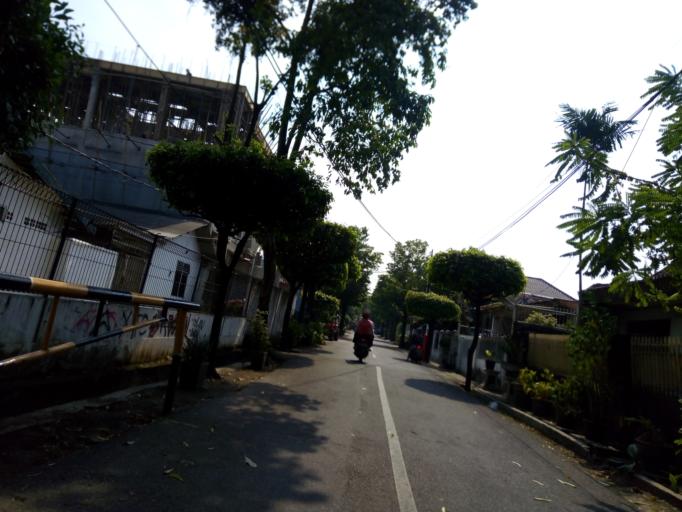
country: ID
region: Jakarta Raya
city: Jakarta
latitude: -6.2105
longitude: 106.8343
